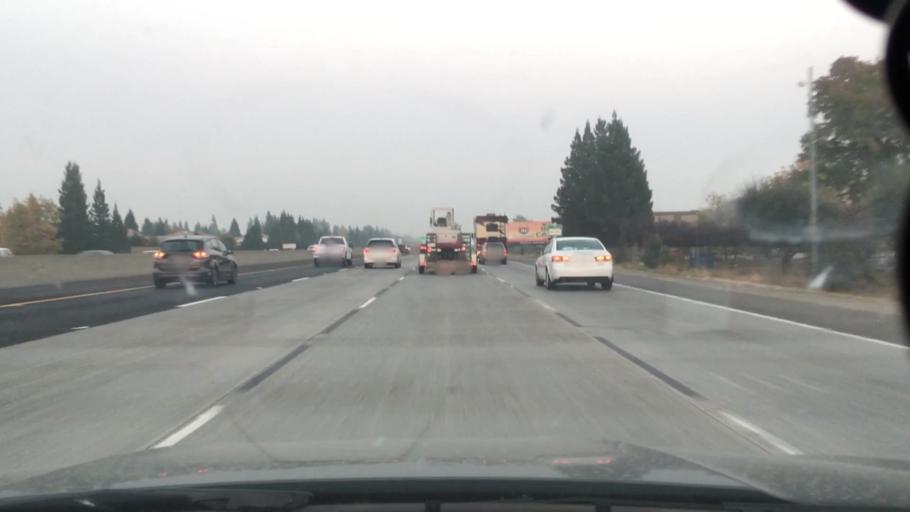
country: US
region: California
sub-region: Sacramento County
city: Gold River
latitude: 38.6154
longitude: -121.2534
